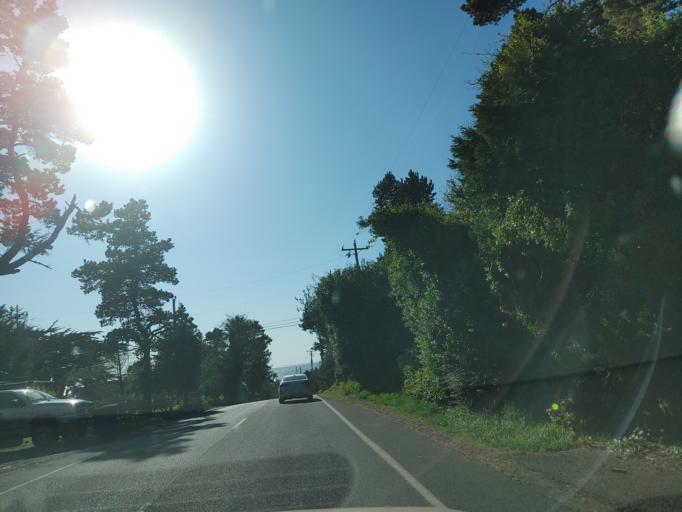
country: US
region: Oregon
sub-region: Lincoln County
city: Depoe Bay
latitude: 44.7471
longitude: -124.0597
